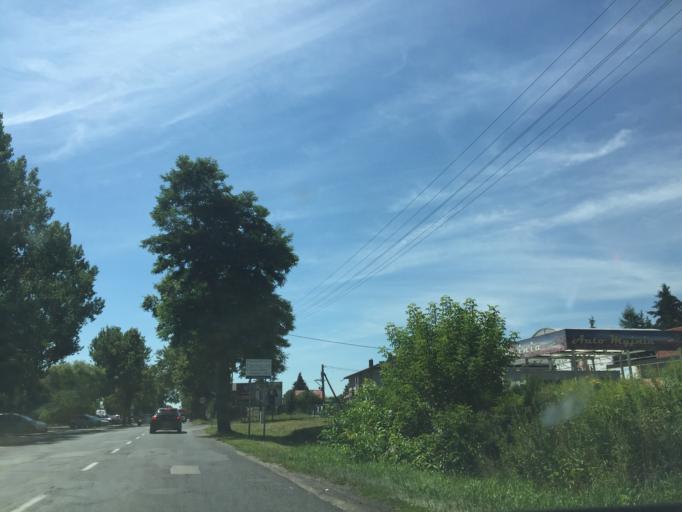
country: PL
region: Lodz Voivodeship
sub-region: Piotrkow Trybunalski
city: Piotrkow Trybunalski
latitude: 51.4206
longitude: 19.7132
